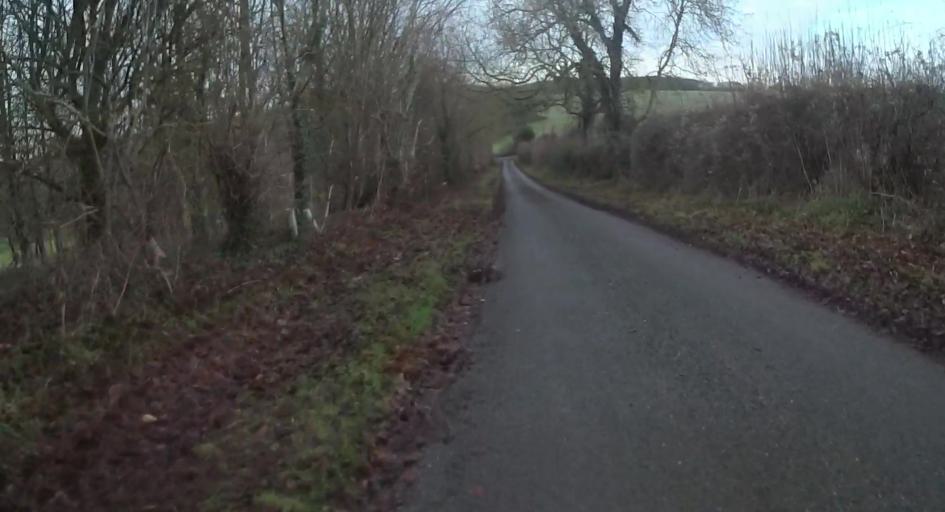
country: GB
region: England
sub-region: Hampshire
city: Kingsclere
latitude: 51.2888
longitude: -1.1947
